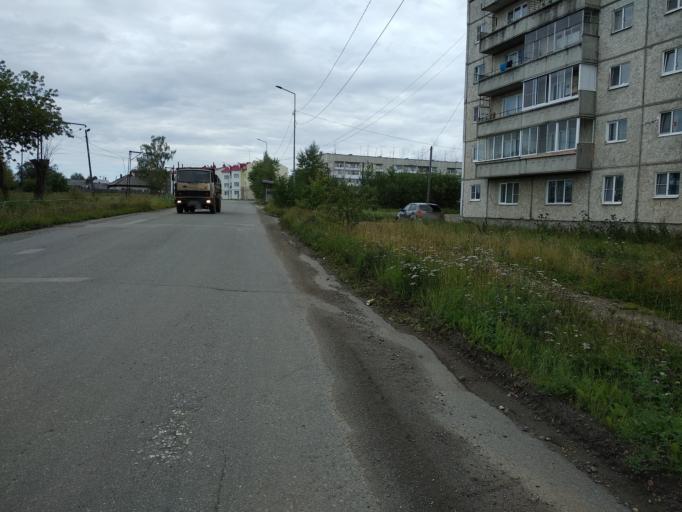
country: RU
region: Sverdlovsk
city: Volchansk
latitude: 59.9365
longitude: 60.0698
